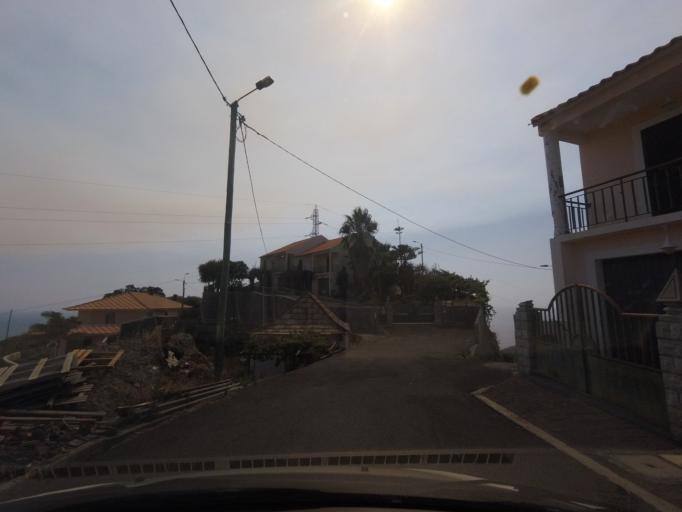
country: PT
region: Madeira
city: Ribeira Brava
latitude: 32.6806
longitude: -17.0693
